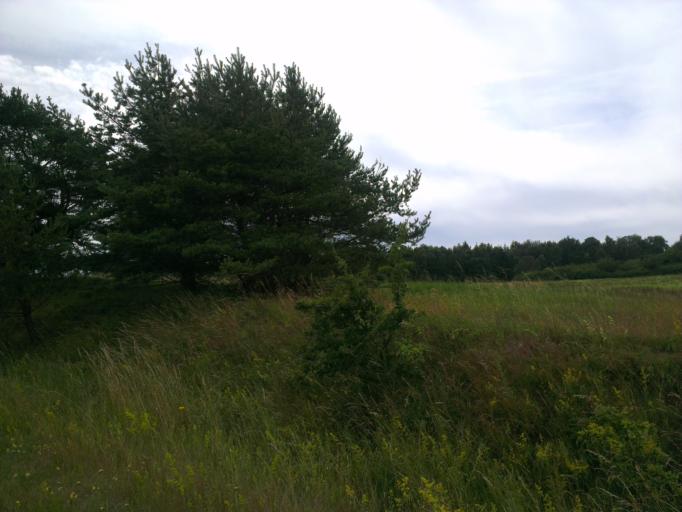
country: DK
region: Capital Region
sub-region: Frederikssund Kommune
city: Jaegerspris
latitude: 55.8998
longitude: 11.9389
